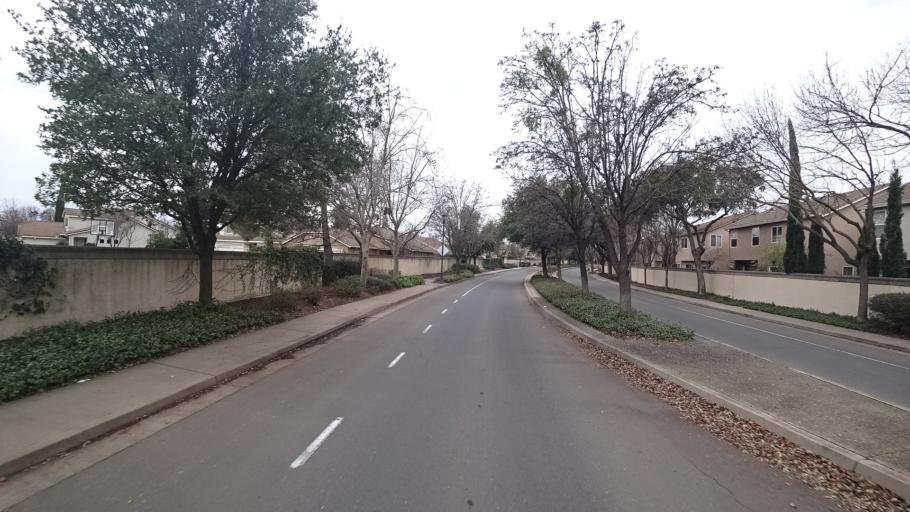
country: US
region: California
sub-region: Yolo County
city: Davis
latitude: 38.5554
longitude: -121.7065
